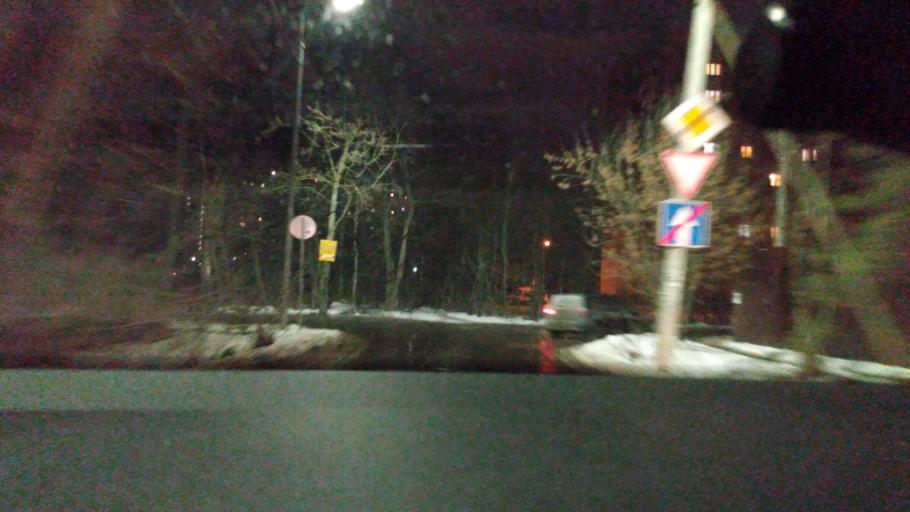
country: RU
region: Moskovskaya
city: Saltykovka
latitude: 55.7556
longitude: 37.9471
